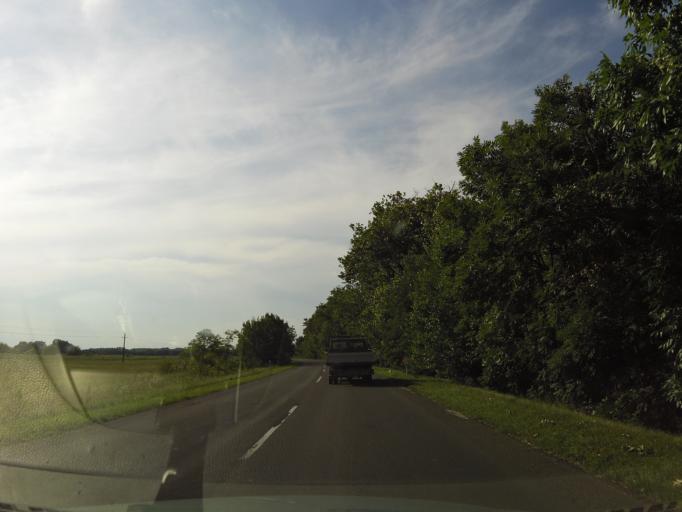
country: HU
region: Csongrad
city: Szatymaz
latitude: 46.3870
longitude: 20.0361
